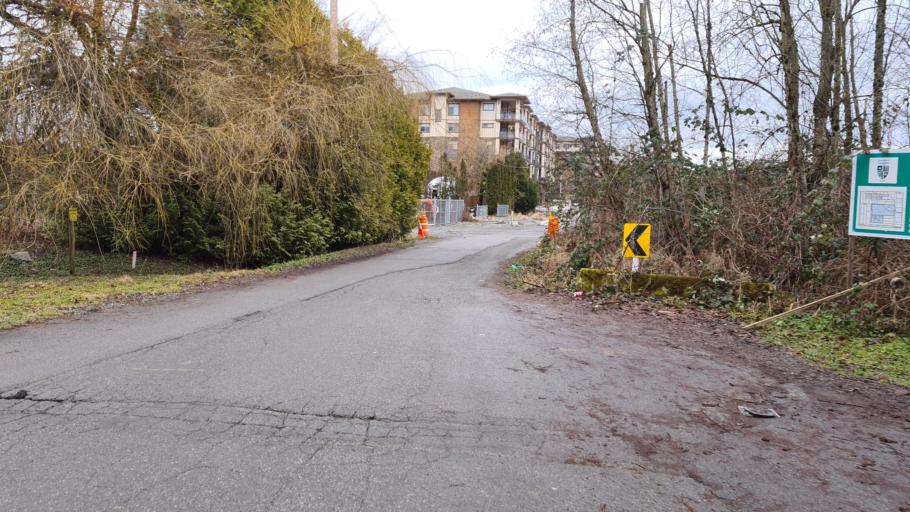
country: CA
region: British Columbia
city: Walnut Grove
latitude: 49.1444
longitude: -122.6517
